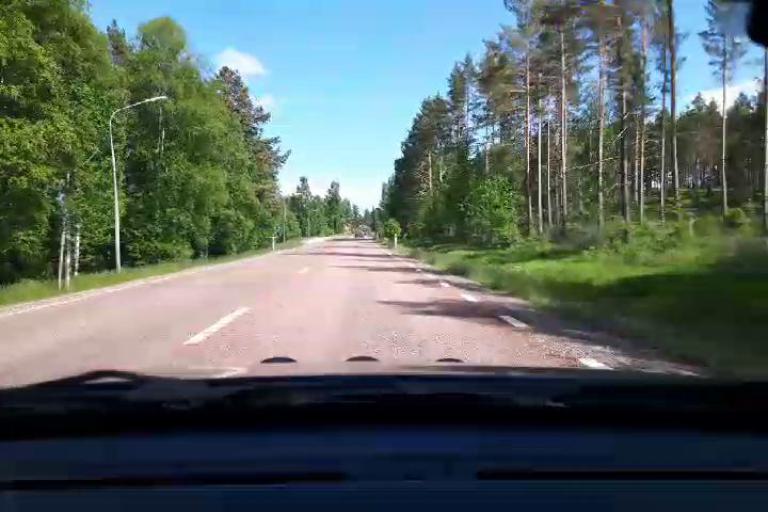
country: SE
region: Gaevleborg
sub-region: Hudiksvalls Kommun
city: Delsbo
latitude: 61.8015
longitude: 16.4839
